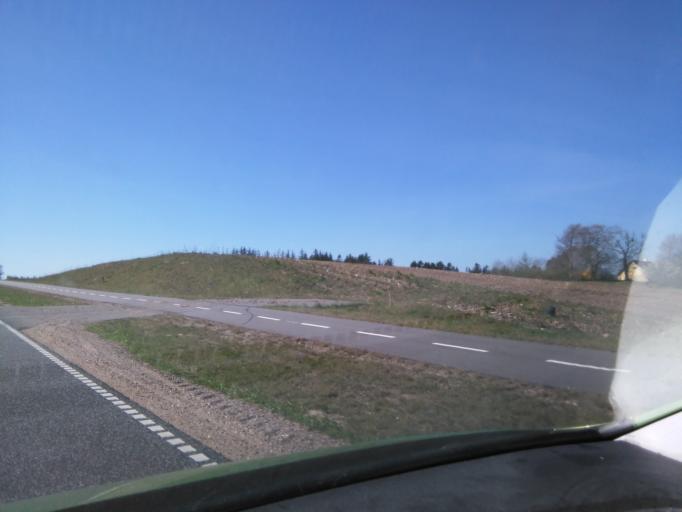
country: DK
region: South Denmark
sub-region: Billund Kommune
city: Billund
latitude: 55.7859
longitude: 9.1771
